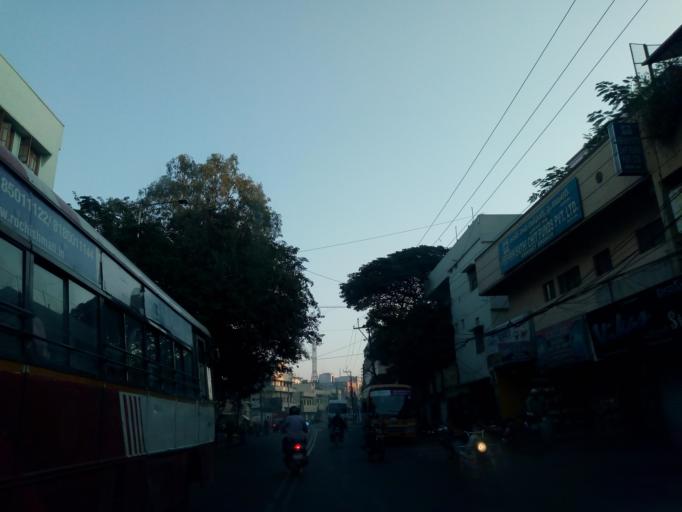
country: IN
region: Telangana
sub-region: Rangareddi
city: Gaddi Annaram
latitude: 17.4071
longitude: 78.5131
